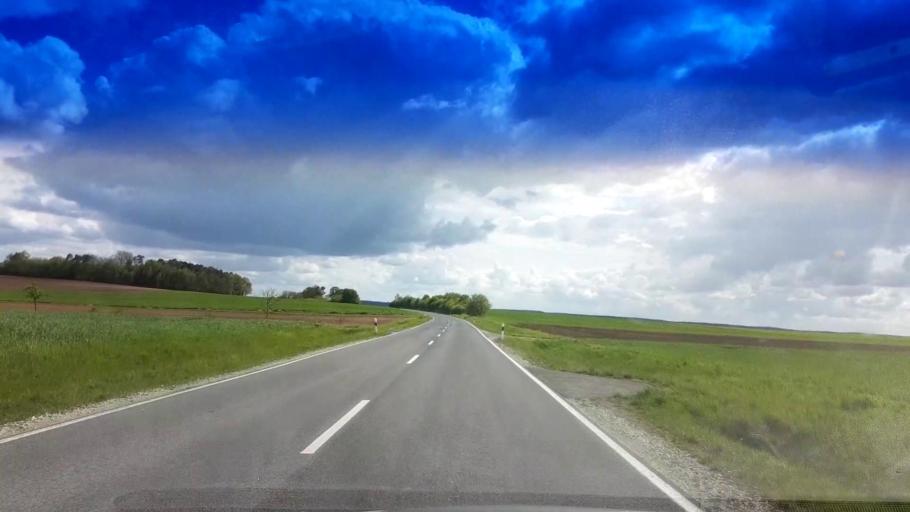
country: DE
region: Bavaria
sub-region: Upper Franconia
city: Stegaurach
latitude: 49.8389
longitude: 10.8386
